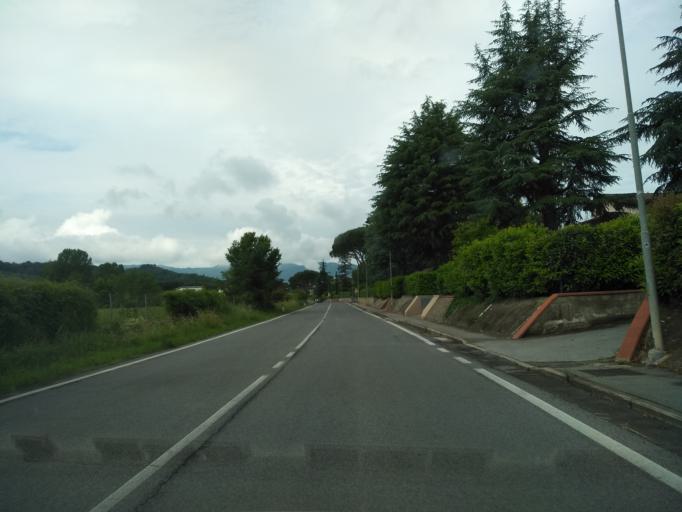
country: IT
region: Tuscany
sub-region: Province of Arezzo
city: Vacchereccia
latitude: 43.5783
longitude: 11.5061
